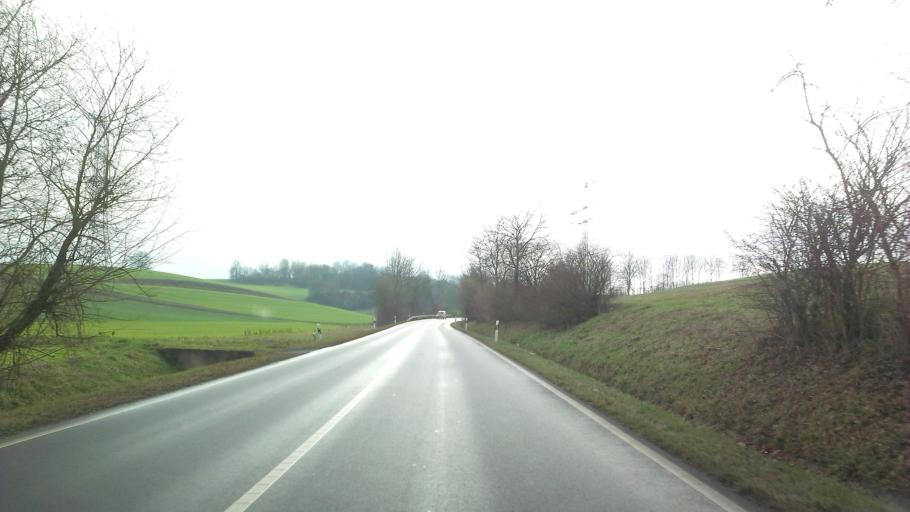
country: DE
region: Baden-Wuerttemberg
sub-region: Karlsruhe Region
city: Meckesheim
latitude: 49.3118
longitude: 8.8045
